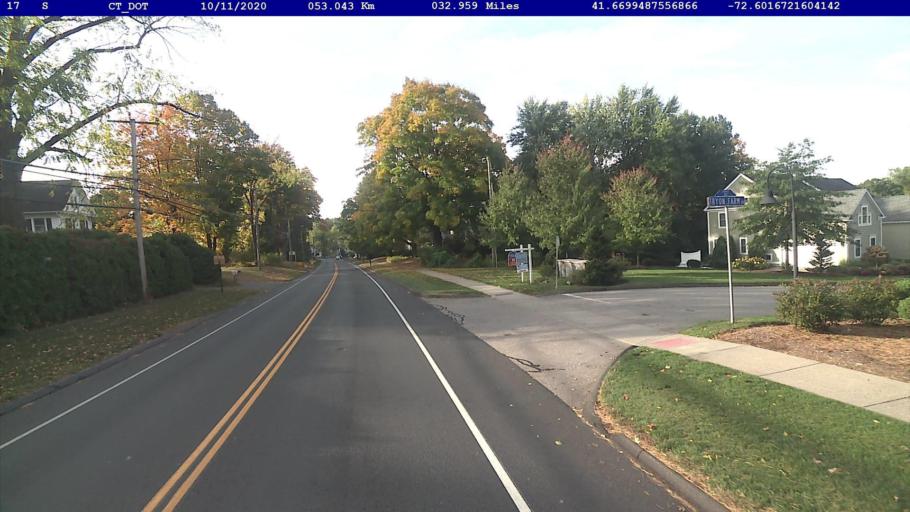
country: US
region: Connecticut
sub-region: Hartford County
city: Glastonbury Center
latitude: 41.6700
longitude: -72.6017
